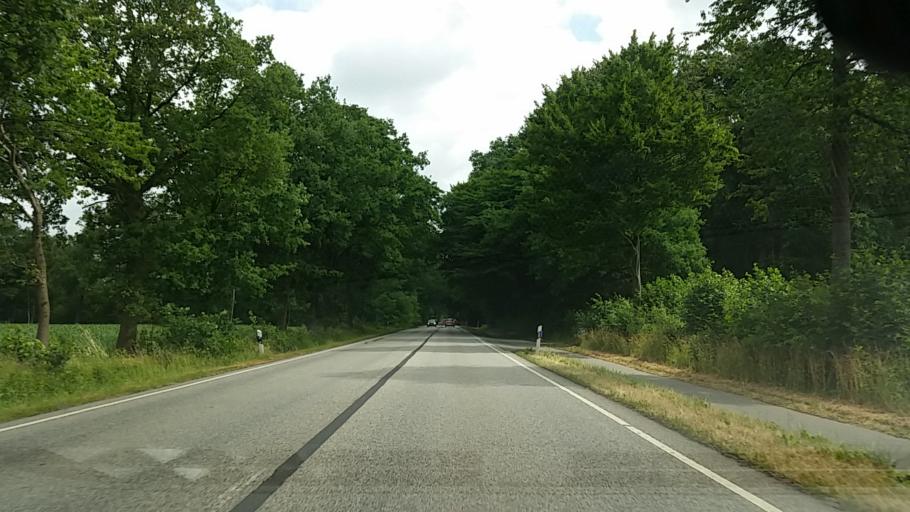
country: DE
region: Schleswig-Holstein
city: Tangstedt
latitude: 53.7333
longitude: 10.1087
